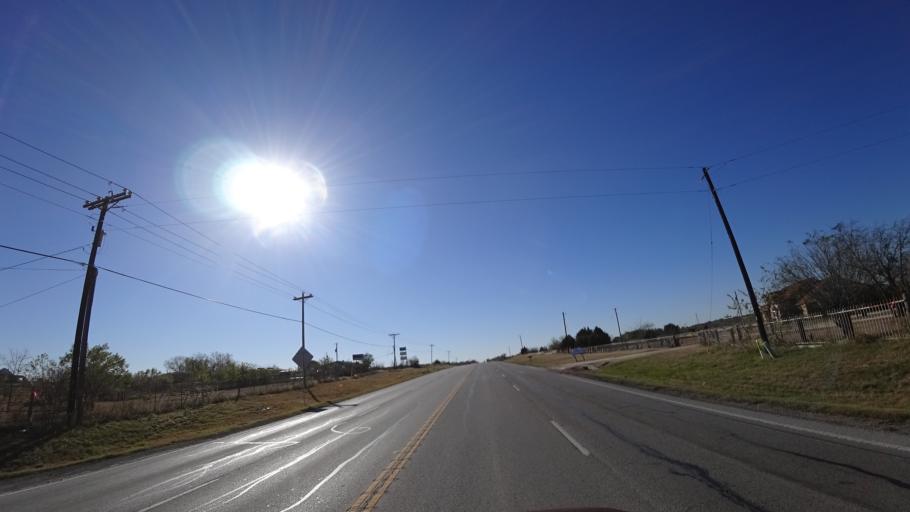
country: US
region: Texas
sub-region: Travis County
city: Onion Creek
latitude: 30.1270
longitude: -97.6958
